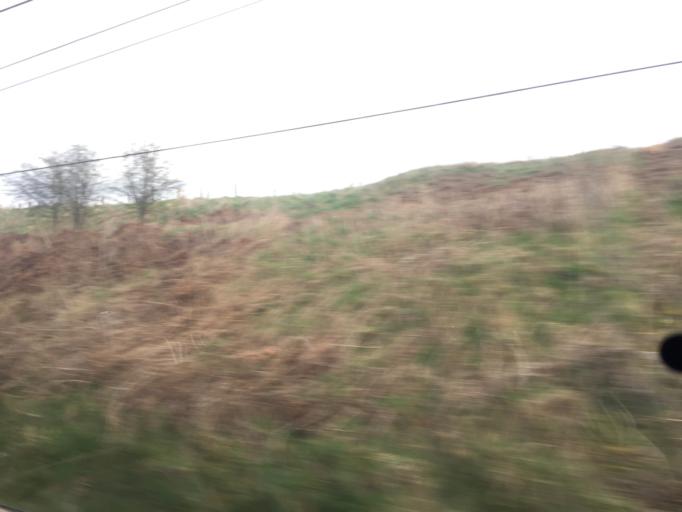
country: GB
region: England
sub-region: Cumbria
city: Scotby
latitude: 54.8424
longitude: -2.8829
